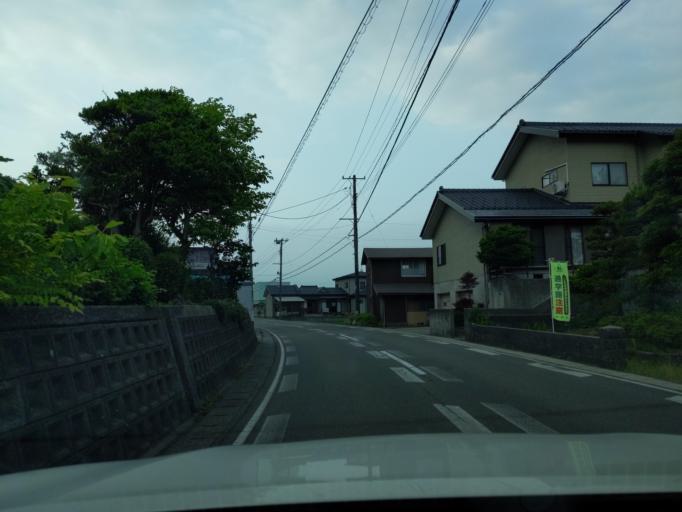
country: JP
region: Niigata
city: Kashiwazaki
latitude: 37.4215
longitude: 138.6177
